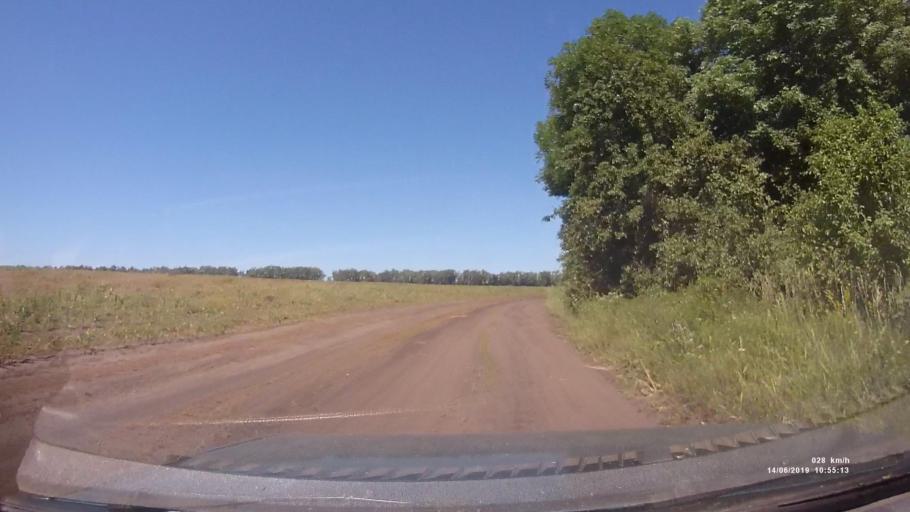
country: RU
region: Rostov
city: Kazanskaya
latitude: 49.8627
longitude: 41.3731
